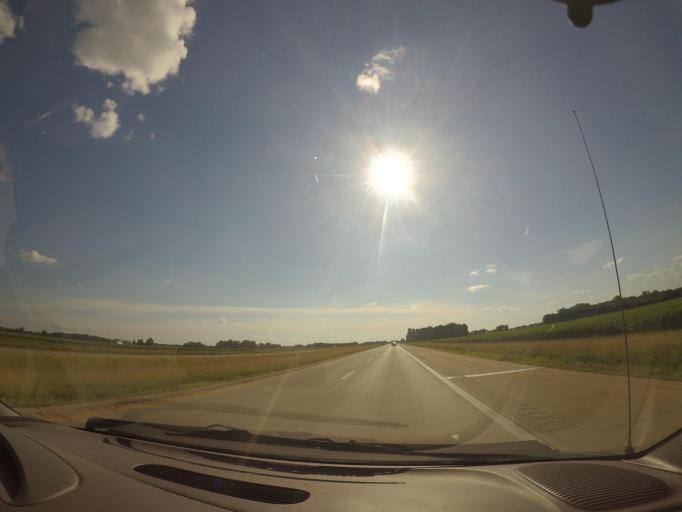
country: US
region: Ohio
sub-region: Lucas County
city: Whitehouse
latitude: 41.4561
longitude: -83.8031
